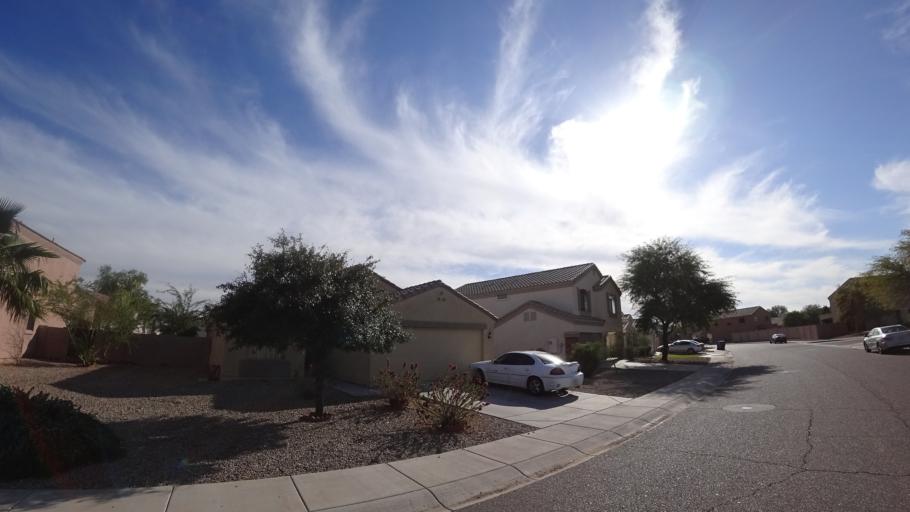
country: US
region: Arizona
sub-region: Maricopa County
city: Tolleson
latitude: 33.4328
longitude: -112.2870
